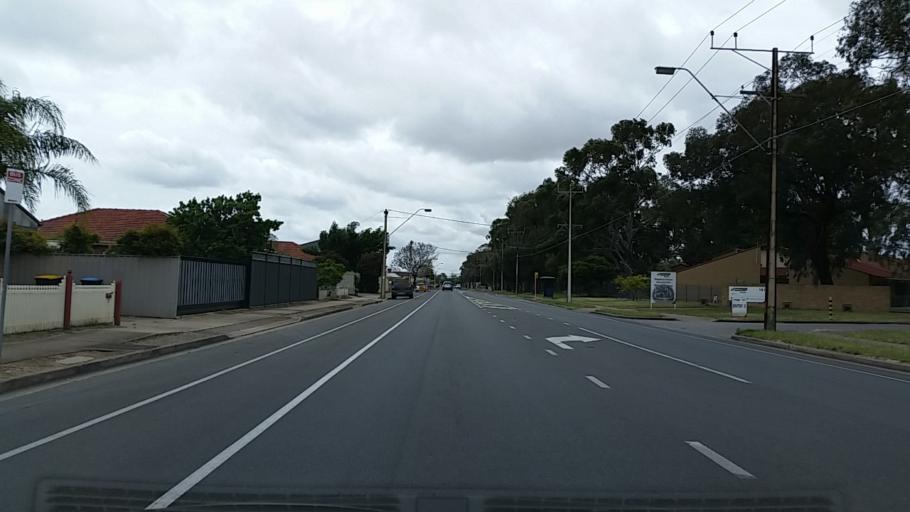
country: AU
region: South Australia
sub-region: Charles Sturt
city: Woodville
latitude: -34.8689
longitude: 138.5658
